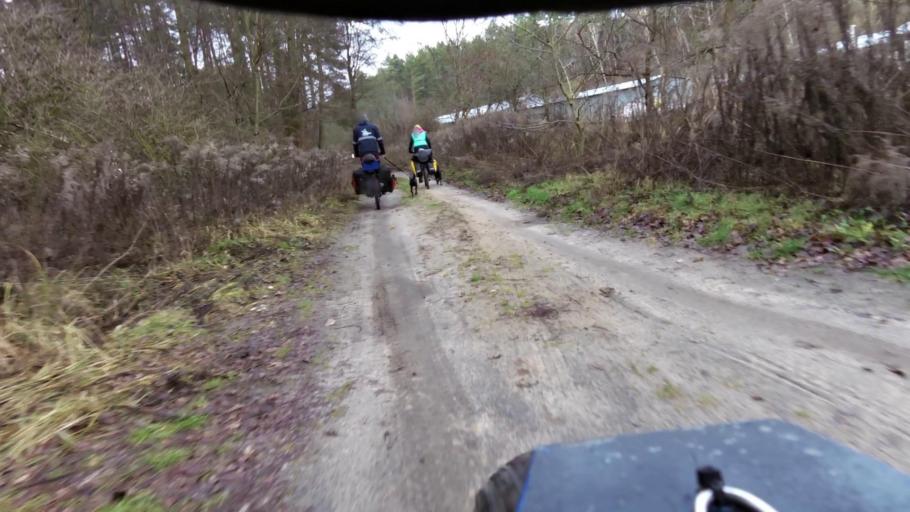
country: PL
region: Lubusz
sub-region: Powiat gorzowski
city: Jenin
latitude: 52.7129
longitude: 15.1301
